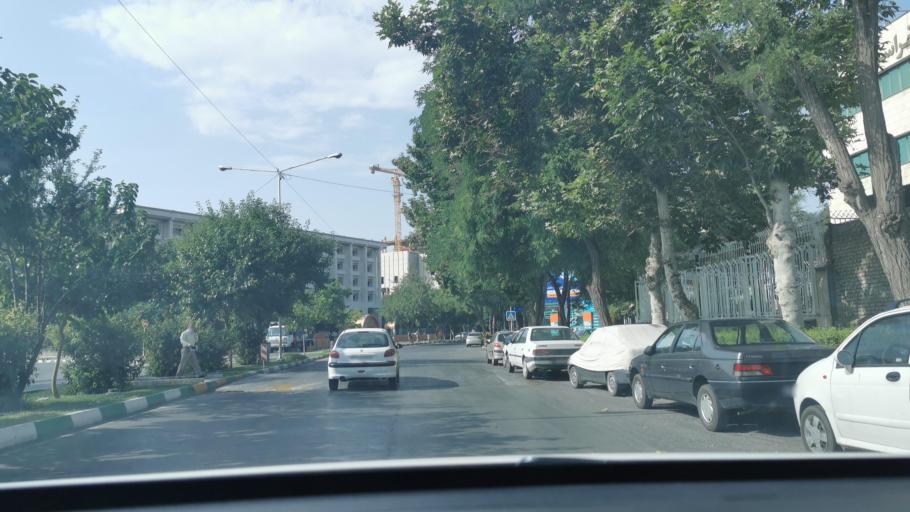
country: IR
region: Razavi Khorasan
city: Mashhad
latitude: 36.3214
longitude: 59.5631
